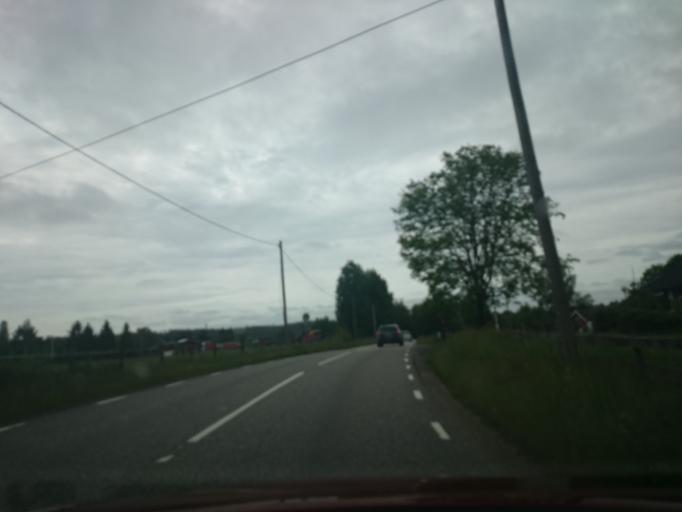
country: SE
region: Vaestra Goetaland
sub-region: Harryda Kommun
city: Hindas
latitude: 57.6987
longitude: 12.3504
